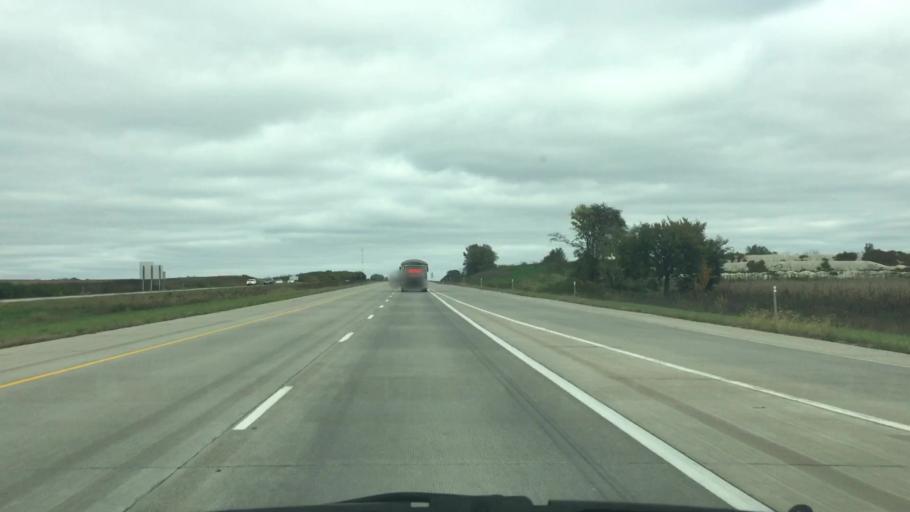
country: US
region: Iowa
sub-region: Warren County
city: Norwalk
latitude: 41.3668
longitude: -93.7801
